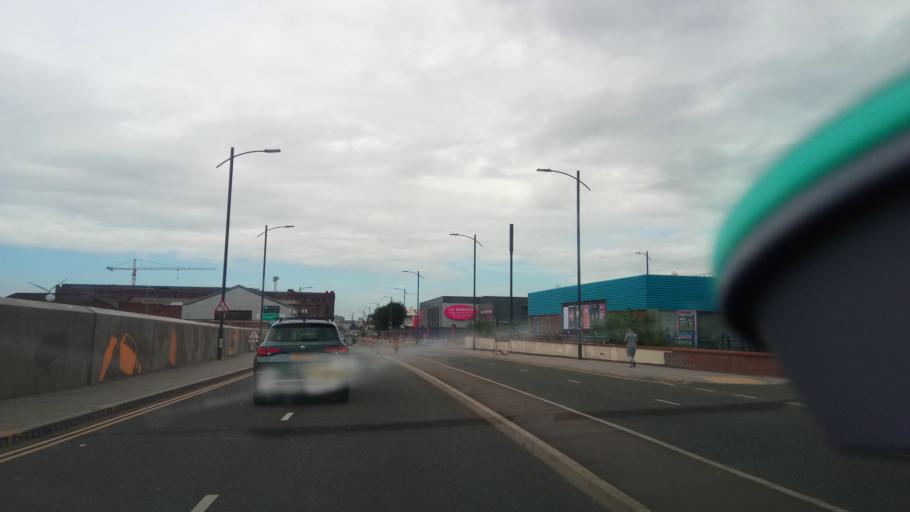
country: GB
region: England
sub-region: Liverpool
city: Liverpool
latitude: 53.4154
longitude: -2.9963
